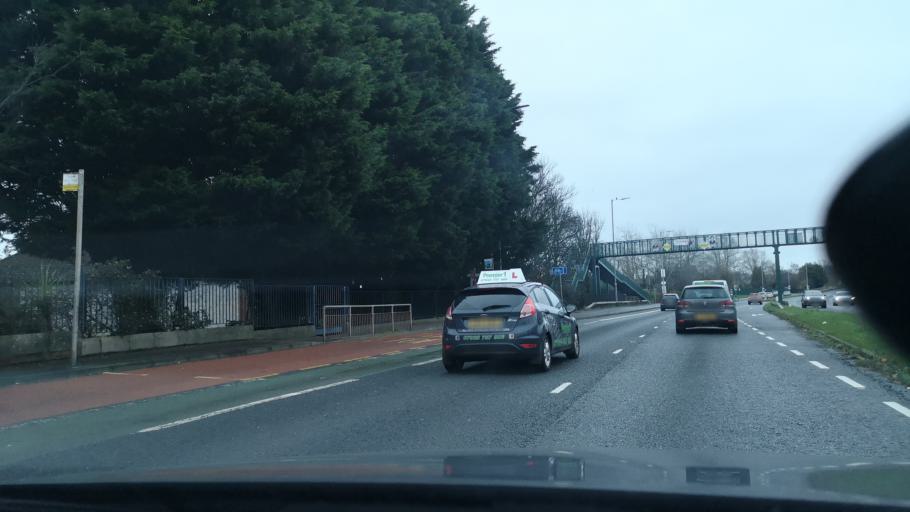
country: GB
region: Northern Ireland
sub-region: Castlereagh District
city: Castlereagh
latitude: 54.5659
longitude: -5.9034
